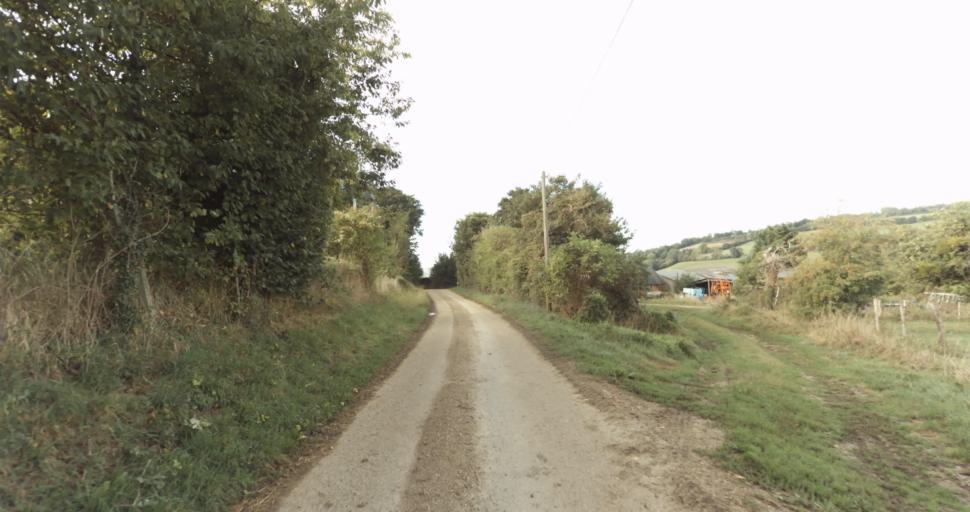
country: FR
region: Lower Normandy
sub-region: Departement de l'Orne
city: Vimoutiers
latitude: 48.8718
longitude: 0.2314
